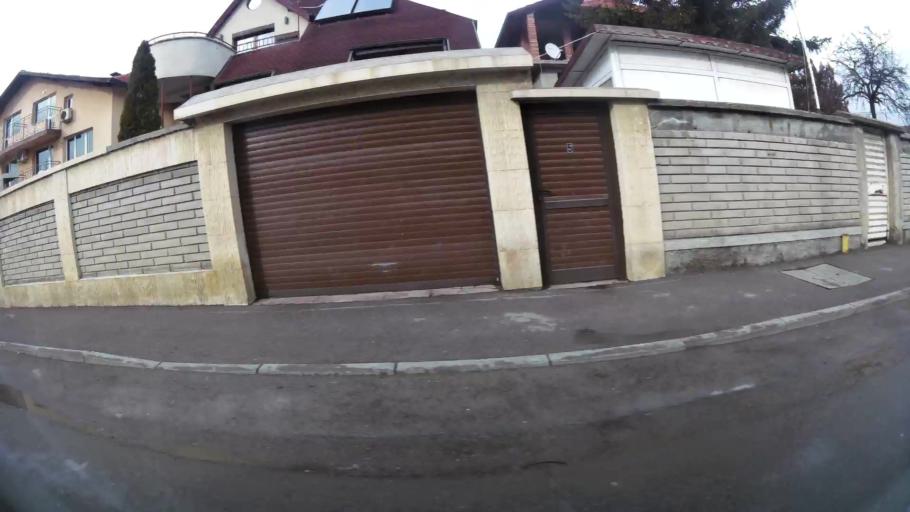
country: BG
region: Sofiya
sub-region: Obshtina Bozhurishte
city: Bozhurishte
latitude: 42.7430
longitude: 23.2674
